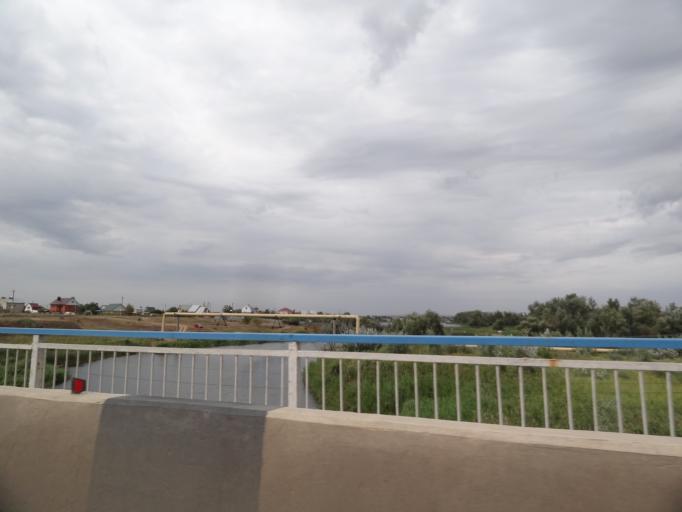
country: RU
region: Saratov
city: Shumeyka
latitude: 51.5216
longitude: 46.2584
